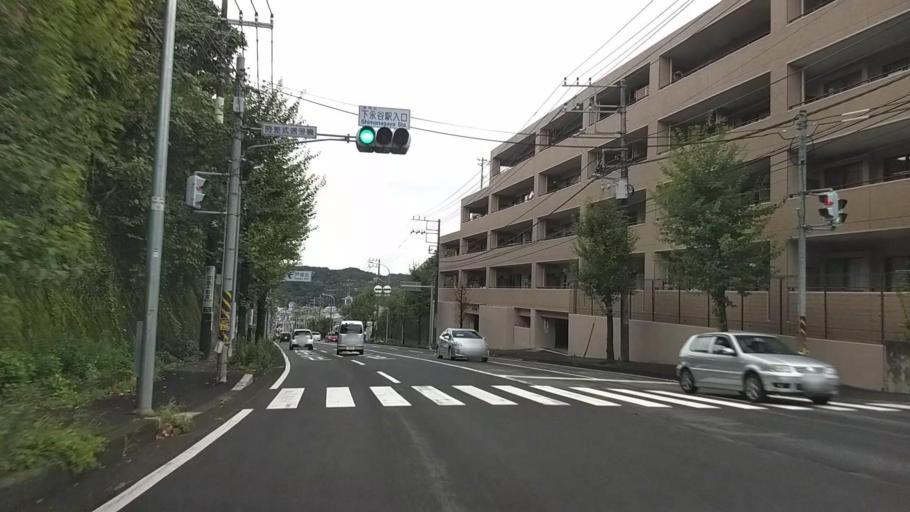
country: JP
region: Kanagawa
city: Kamakura
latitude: 35.4008
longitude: 139.5570
